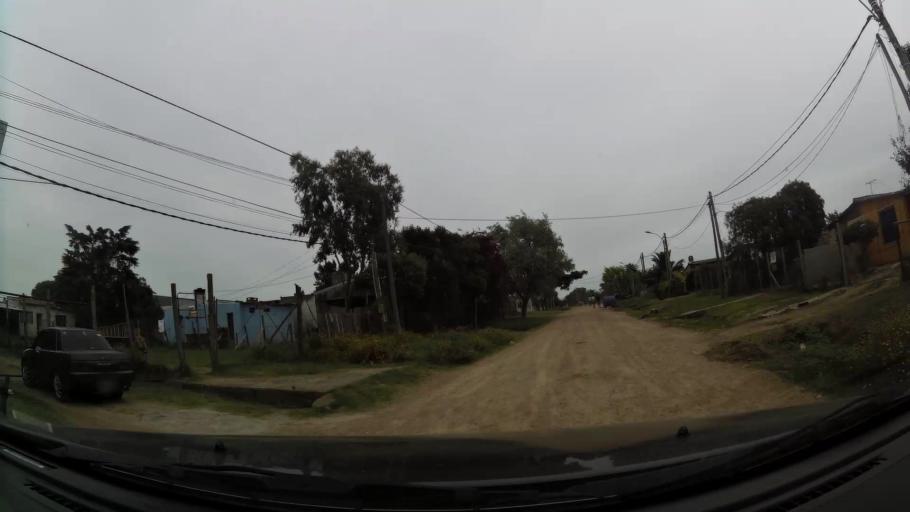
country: UY
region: Canelones
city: Las Piedras
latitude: -34.7388
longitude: -56.2150
